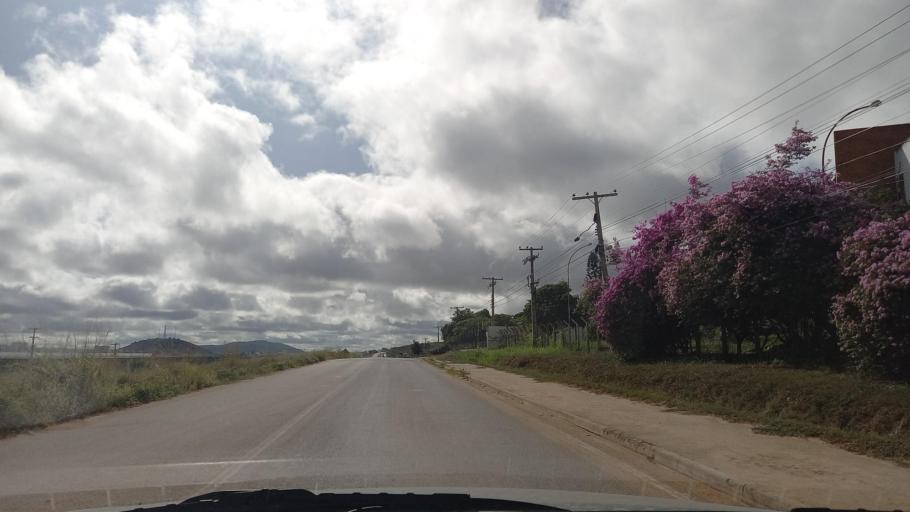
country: BR
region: Pernambuco
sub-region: Caruaru
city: Caruaru
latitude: -8.3035
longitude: -36.0052
